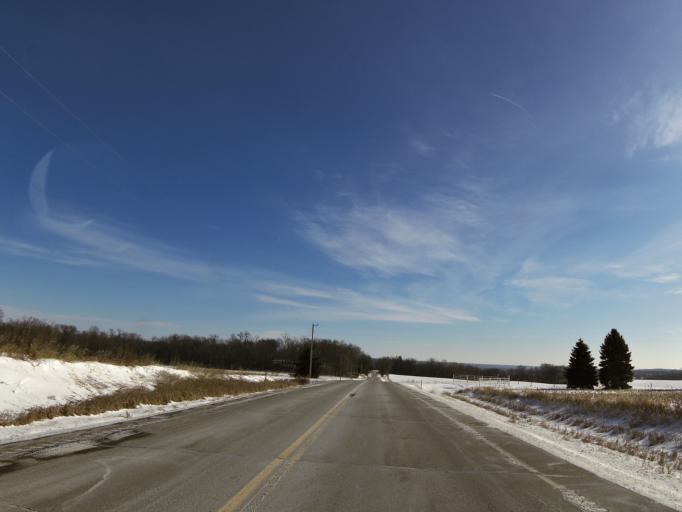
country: US
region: Minnesota
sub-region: Dakota County
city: Hastings
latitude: 44.7566
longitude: -92.9002
